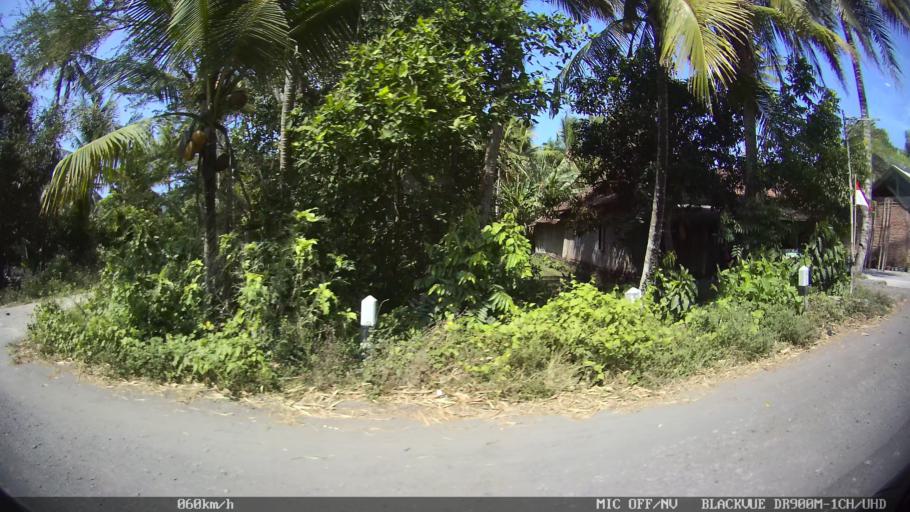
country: ID
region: Daerah Istimewa Yogyakarta
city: Srandakan
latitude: -7.9393
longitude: 110.1587
